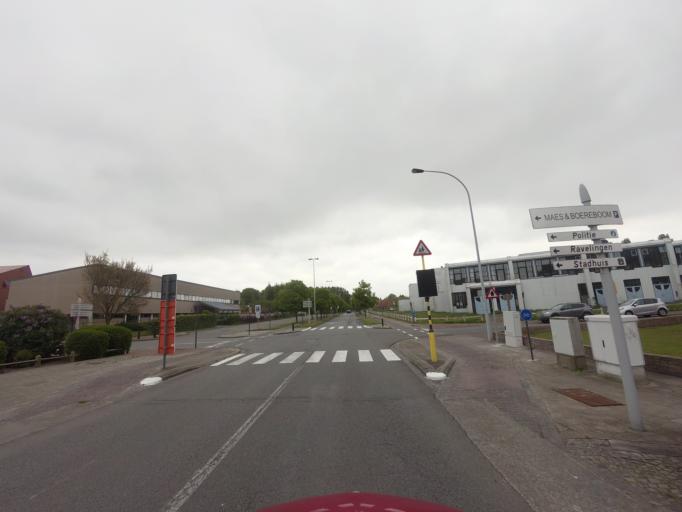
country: BE
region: Flanders
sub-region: Provincie West-Vlaanderen
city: Knokke-Heist
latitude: 51.3359
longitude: 3.2345
